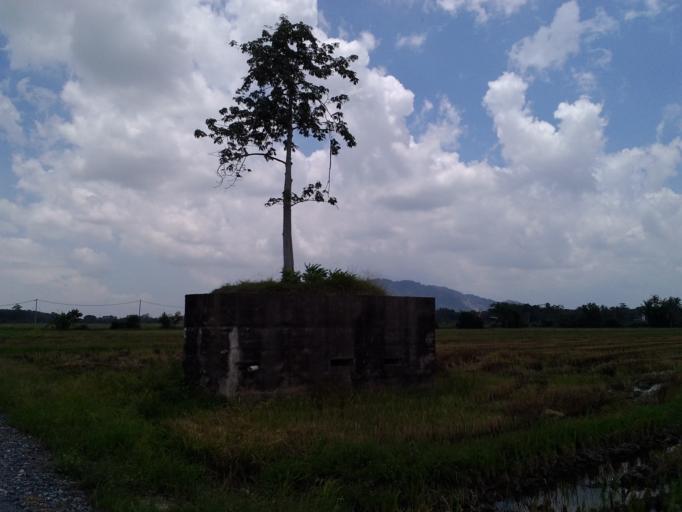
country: MY
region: Kedah
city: Jitra
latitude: 6.2717
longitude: 100.3996
